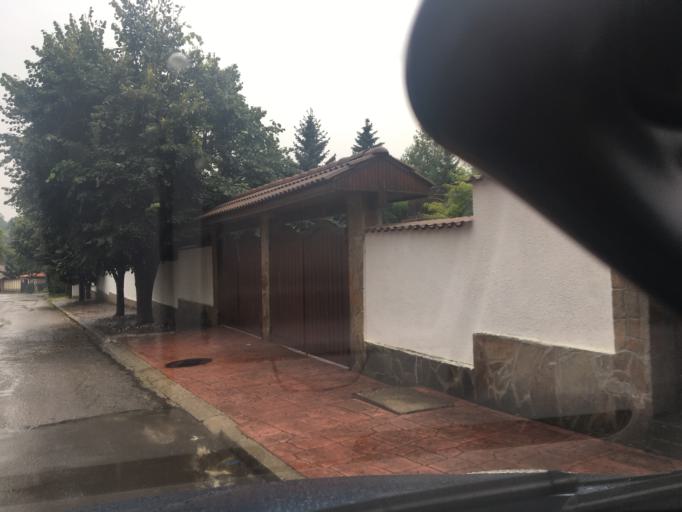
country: BG
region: Sofia-Capital
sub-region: Stolichna Obshtina
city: Sofia
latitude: 42.5864
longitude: 23.3519
